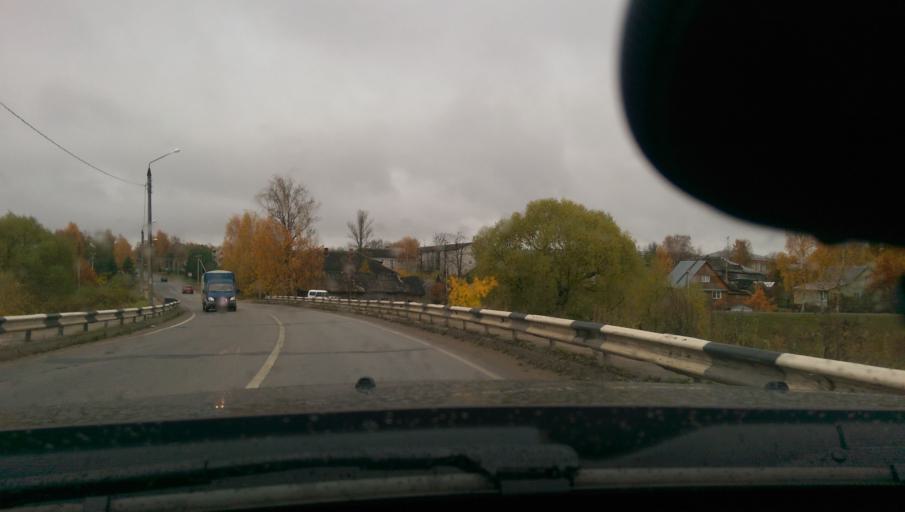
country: RU
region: Jaroslavl
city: Poshekhon'ye
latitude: 58.5054
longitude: 39.1309
